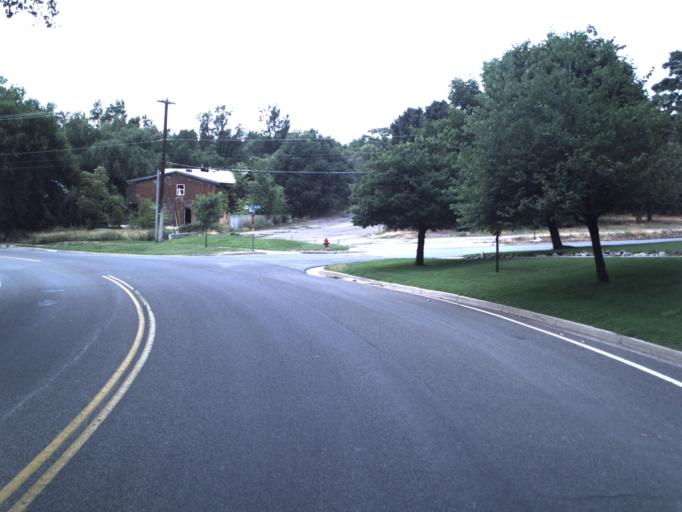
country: US
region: Utah
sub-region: Davis County
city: Farmington
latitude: 40.9898
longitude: -111.8876
